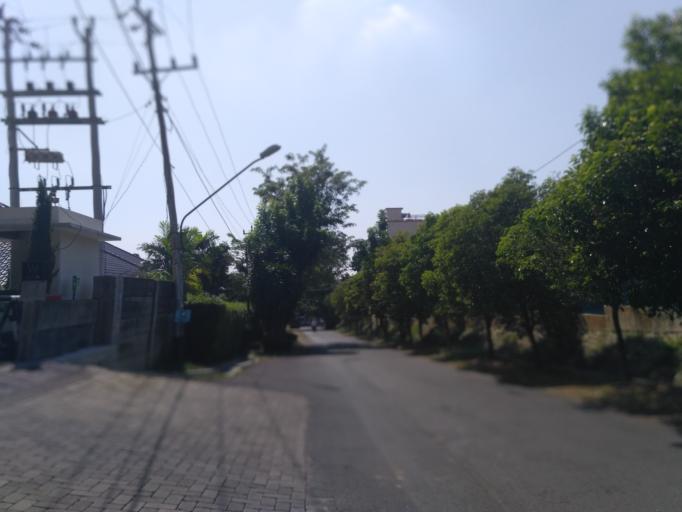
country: ID
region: Central Java
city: Semarang
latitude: -7.0074
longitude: 110.4188
